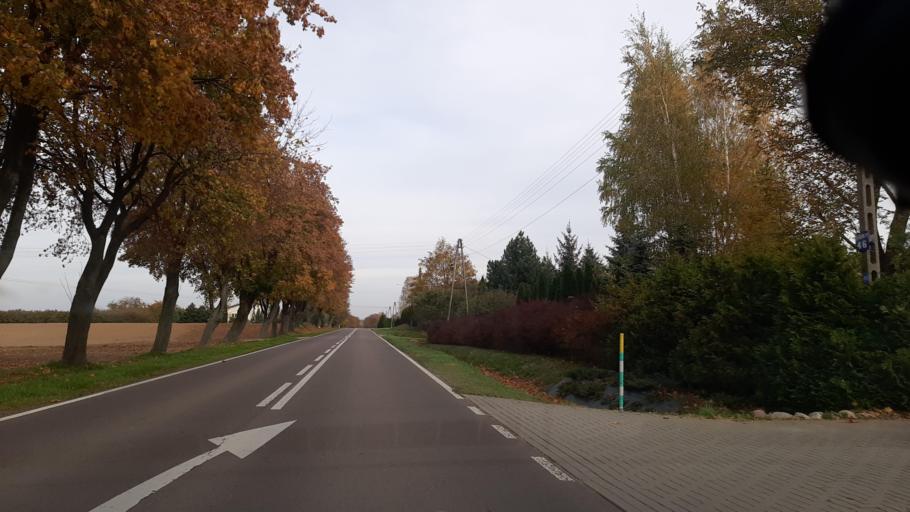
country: PL
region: Lublin Voivodeship
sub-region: Powiat pulawski
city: Markuszow
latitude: 51.3468
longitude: 22.2660
